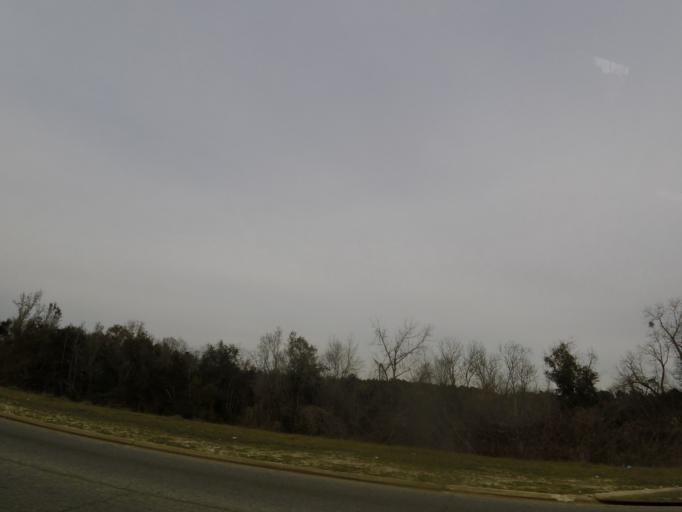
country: US
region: Georgia
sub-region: Decatur County
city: Bainbridge
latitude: 30.9098
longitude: -84.5783
